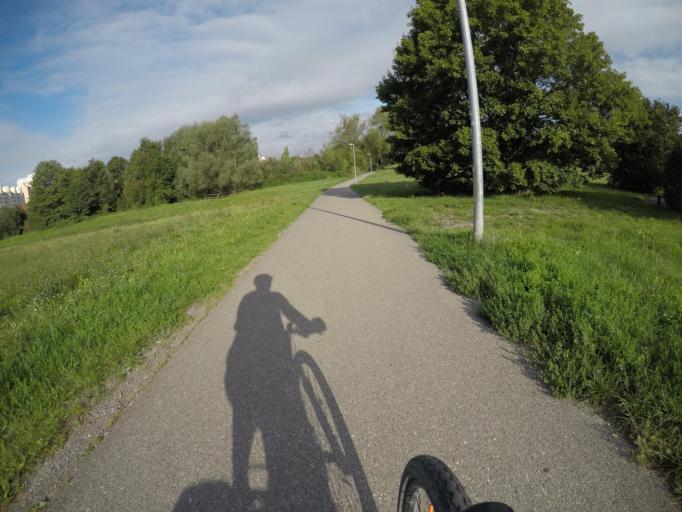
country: DE
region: Baden-Wuerttemberg
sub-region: Regierungsbezirk Stuttgart
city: Magstadt
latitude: 48.7246
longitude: 8.9906
